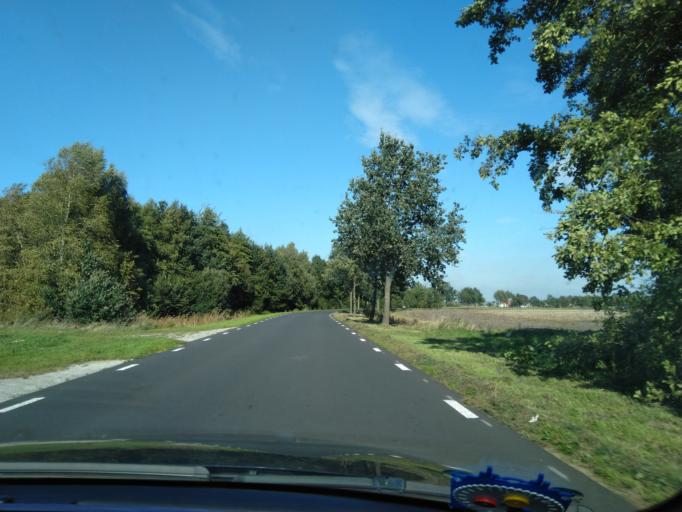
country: NL
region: Groningen
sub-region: Gemeente Hoogezand-Sappemeer
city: Sappemeer
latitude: 53.0851
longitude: 6.7881
